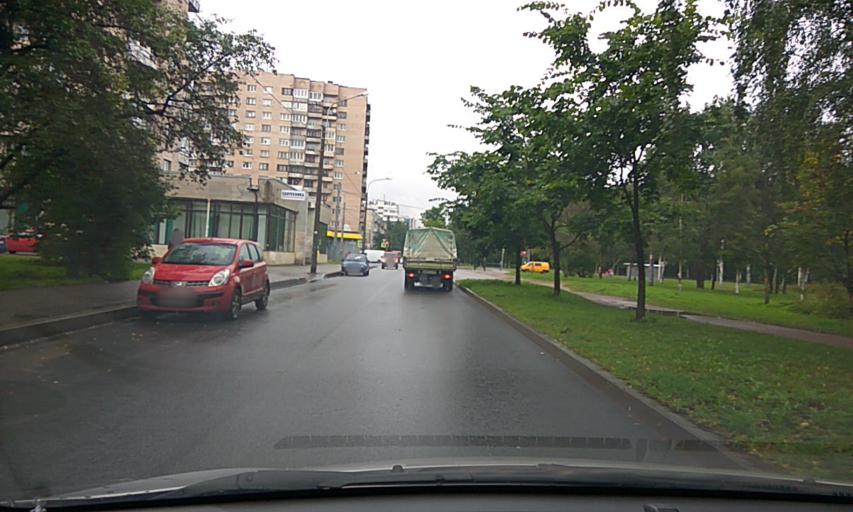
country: RU
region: St.-Petersburg
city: Dachnoye
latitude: 59.8341
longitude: 30.2237
